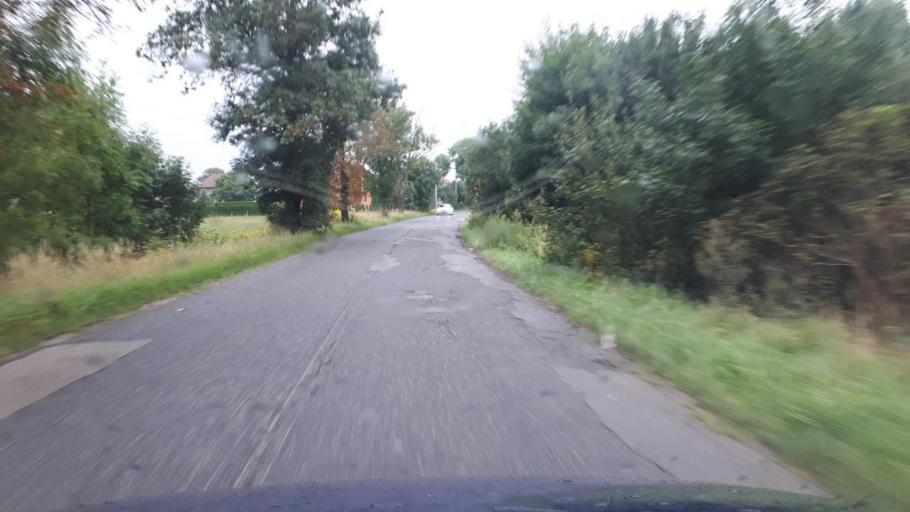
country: PL
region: Silesian Voivodeship
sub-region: Powiat tarnogorski
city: Wieszowa
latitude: 50.3693
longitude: 18.7182
